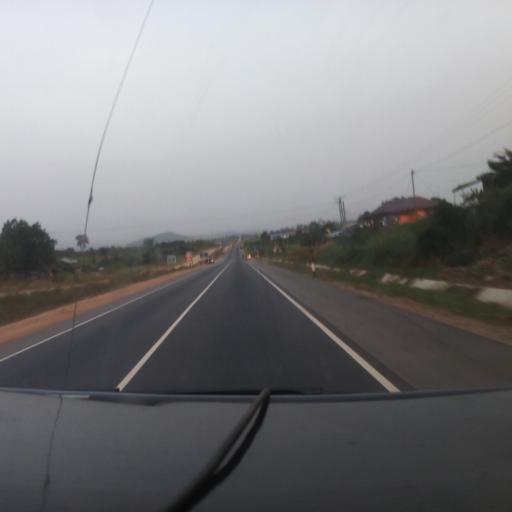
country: GH
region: Eastern
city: Nsawam
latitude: 5.8740
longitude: -0.3700
